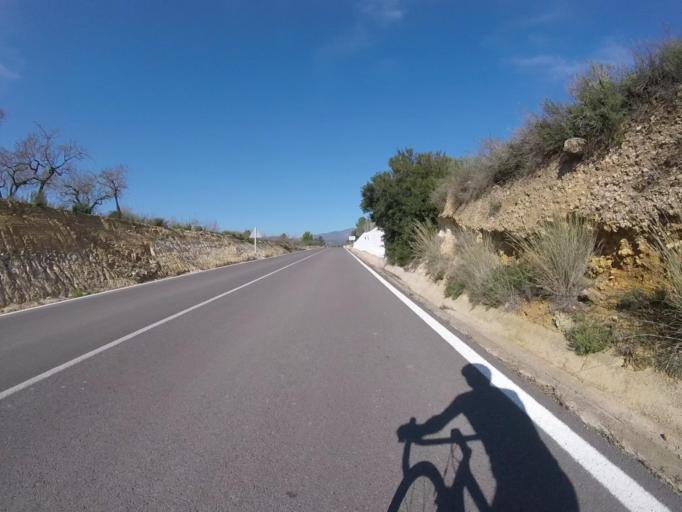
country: ES
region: Valencia
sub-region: Provincia de Castello
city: Cuevas de Vinroma
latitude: 40.2596
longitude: 0.0799
